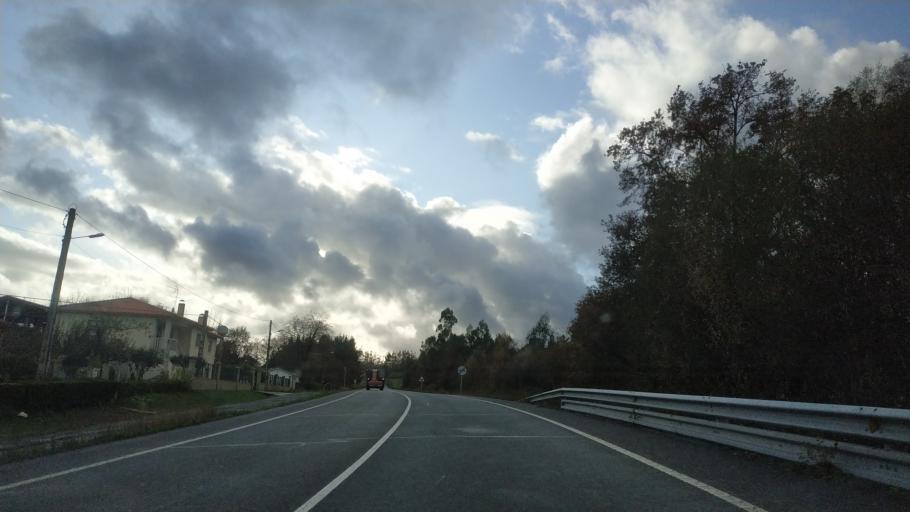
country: ES
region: Galicia
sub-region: Provincia da Coruna
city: Arzua
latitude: 42.8828
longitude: -8.1963
